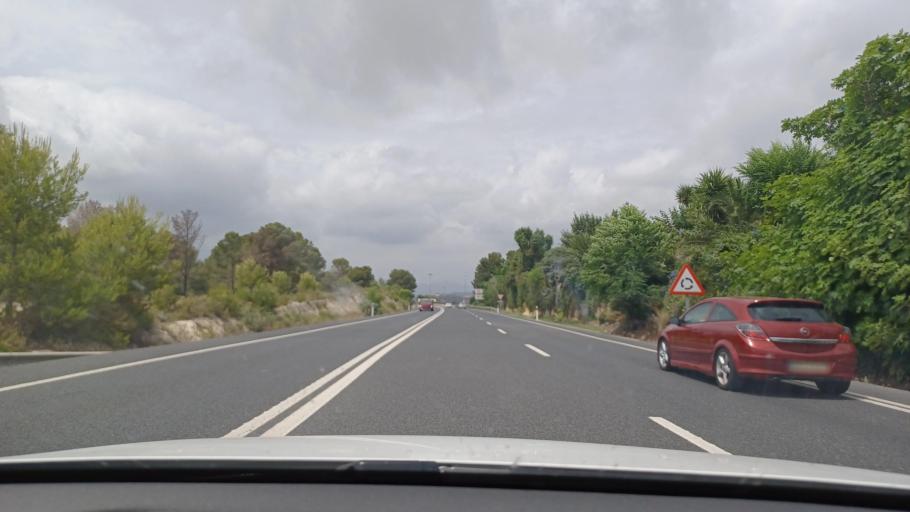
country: ES
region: Catalonia
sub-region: Provincia de Tarragona
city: els Pallaresos
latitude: 41.1602
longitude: 1.2401
